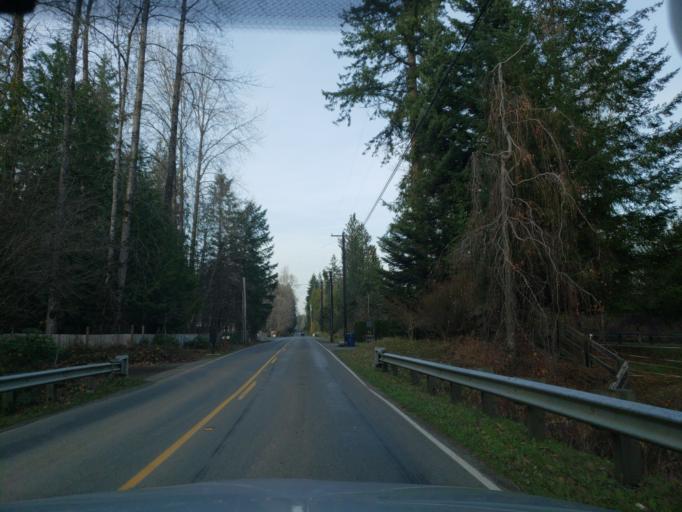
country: US
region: Washington
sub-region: Snohomish County
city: Cathcart
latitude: 47.8192
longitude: -122.0769
